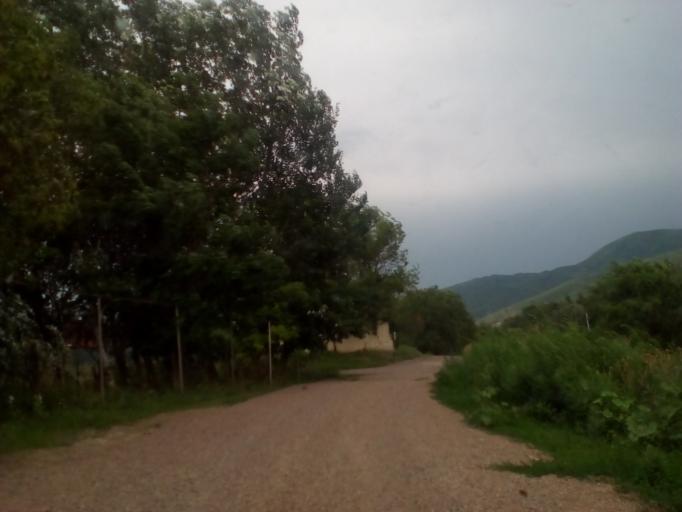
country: KZ
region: Almaty Oblysy
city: Burunday
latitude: 43.1576
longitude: 76.4009
